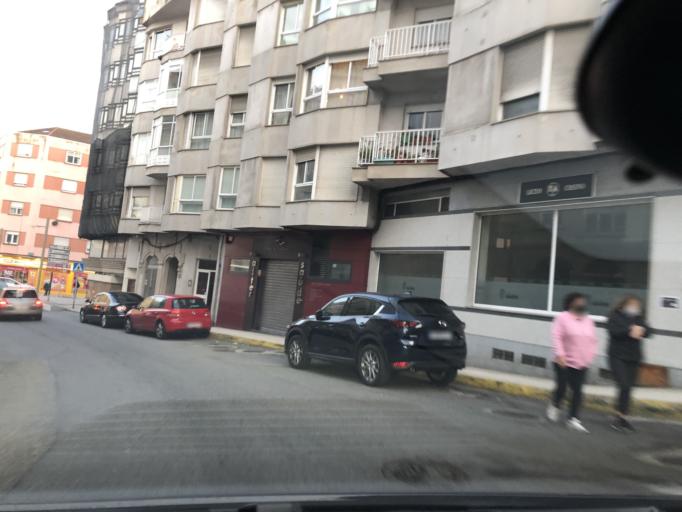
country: ES
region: Galicia
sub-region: Provincia de Pontevedra
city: Marin
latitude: 42.3907
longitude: -8.7057
